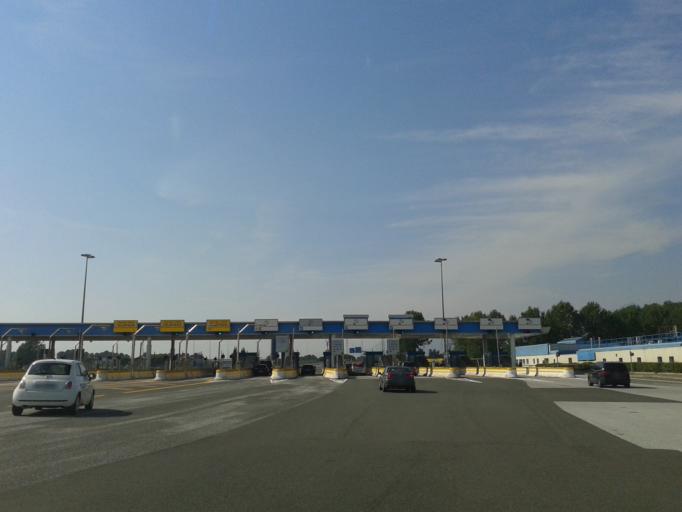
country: IT
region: Tuscany
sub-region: Provincia di Lucca
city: Camaiore
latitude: 43.8924
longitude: 10.2607
